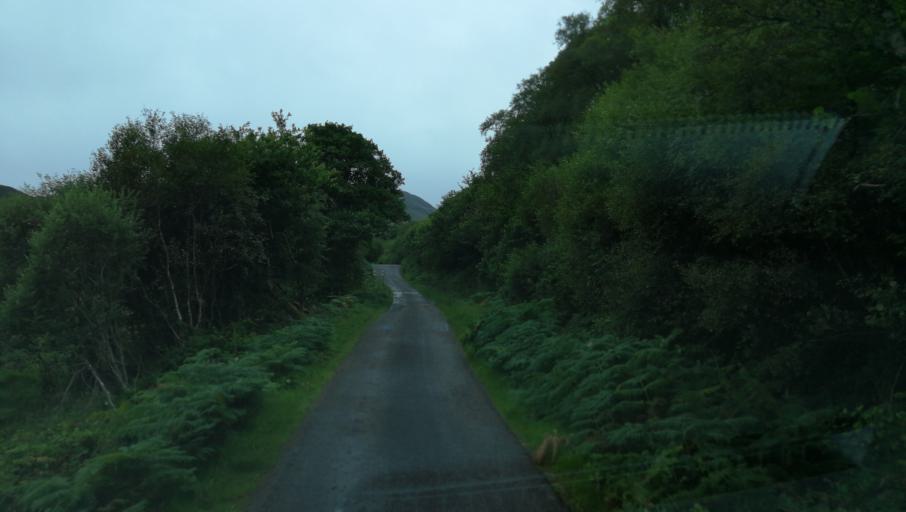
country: GB
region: Scotland
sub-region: Argyll and Bute
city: Isle Of Mull
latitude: 56.7220
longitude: -6.1706
